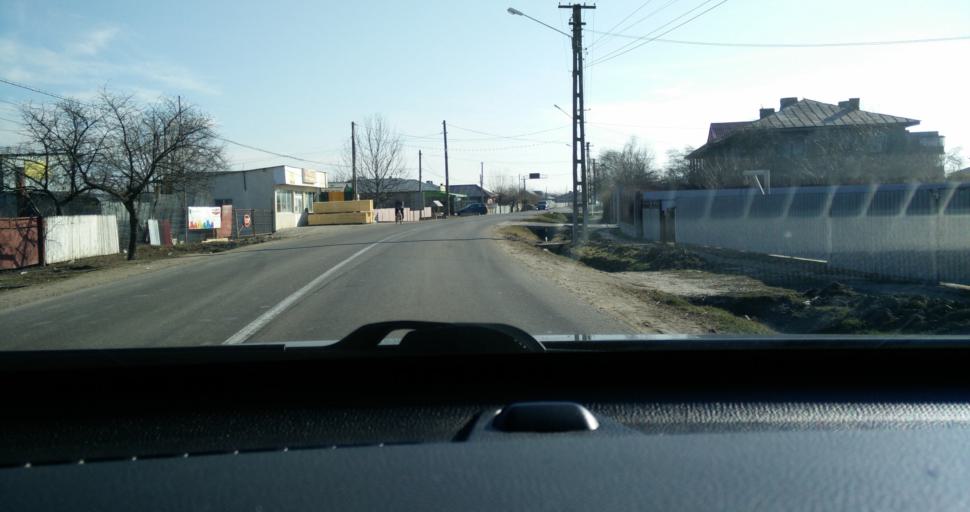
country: RO
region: Vrancea
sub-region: Comuna Nanesti
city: Nanesti
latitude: 45.5508
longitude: 27.5006
